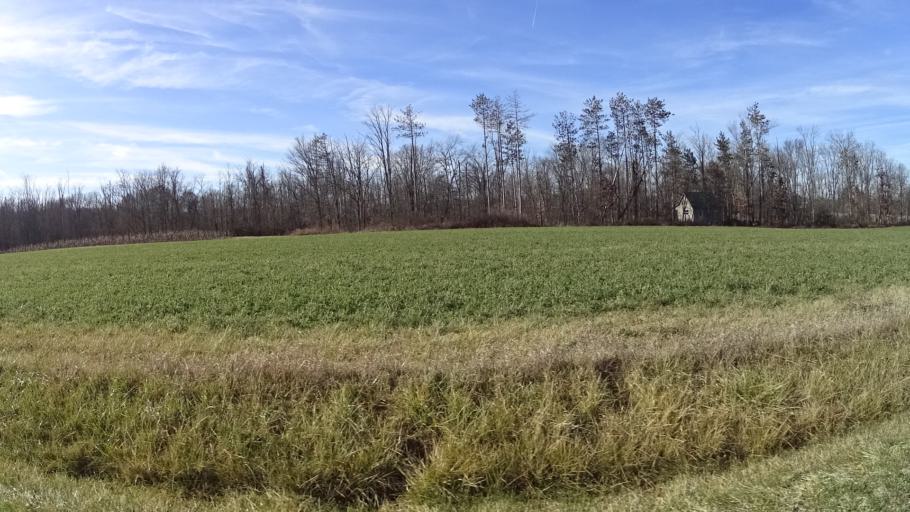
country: US
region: Ohio
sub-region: Lorain County
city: Wellington
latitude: 41.0823
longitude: -82.2402
